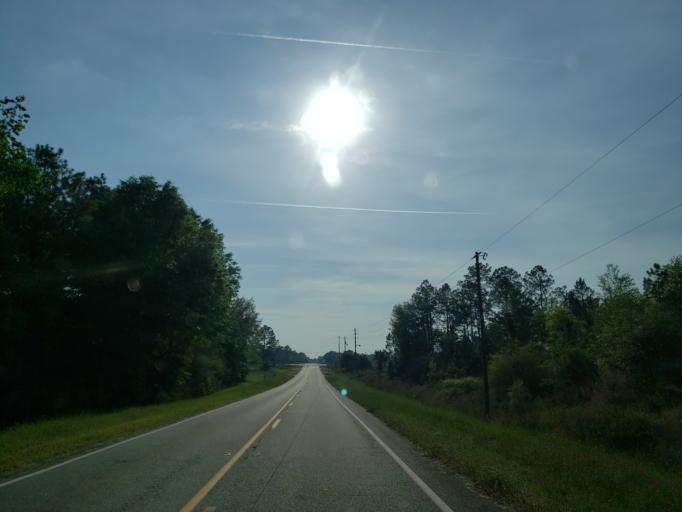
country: US
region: Georgia
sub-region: Tift County
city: Tifton
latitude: 31.5508
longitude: -83.5308
